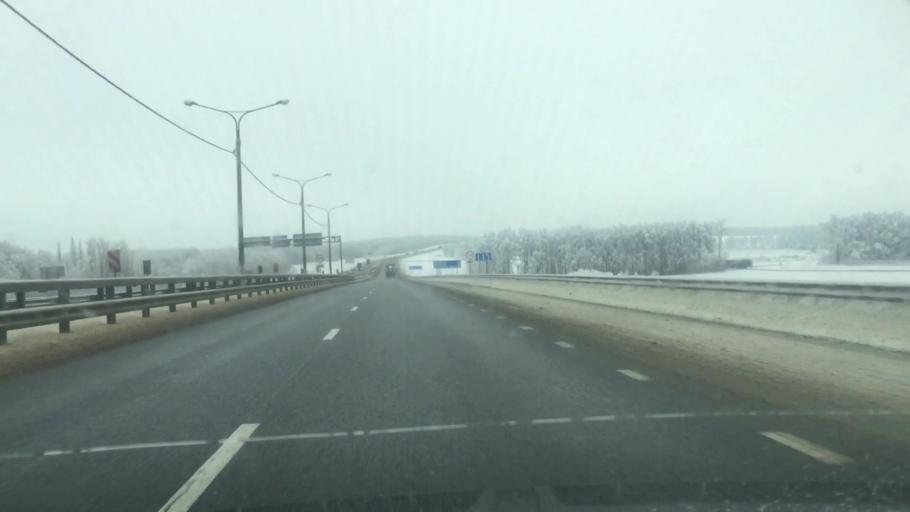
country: RU
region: Lipetsk
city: Yelets
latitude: 52.5410
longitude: 38.7249
